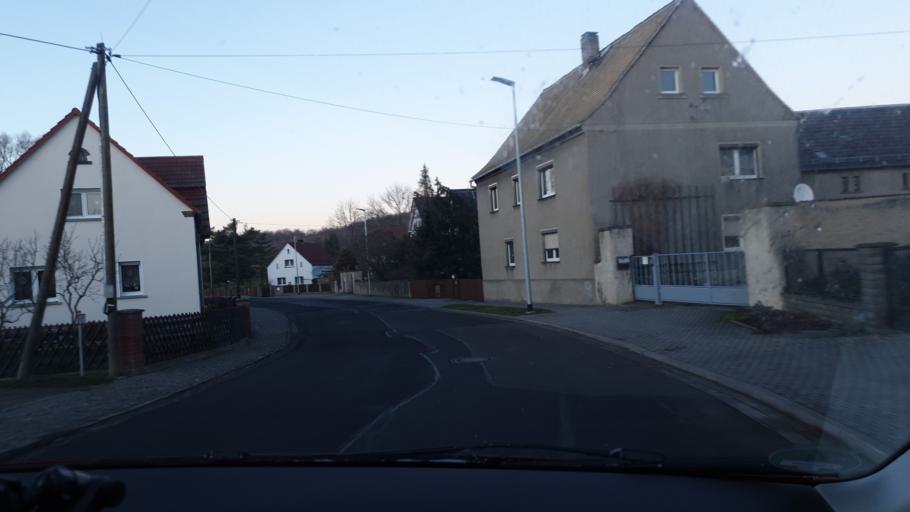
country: DE
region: Saxony
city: Hohburg
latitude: 51.4141
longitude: 12.7812
